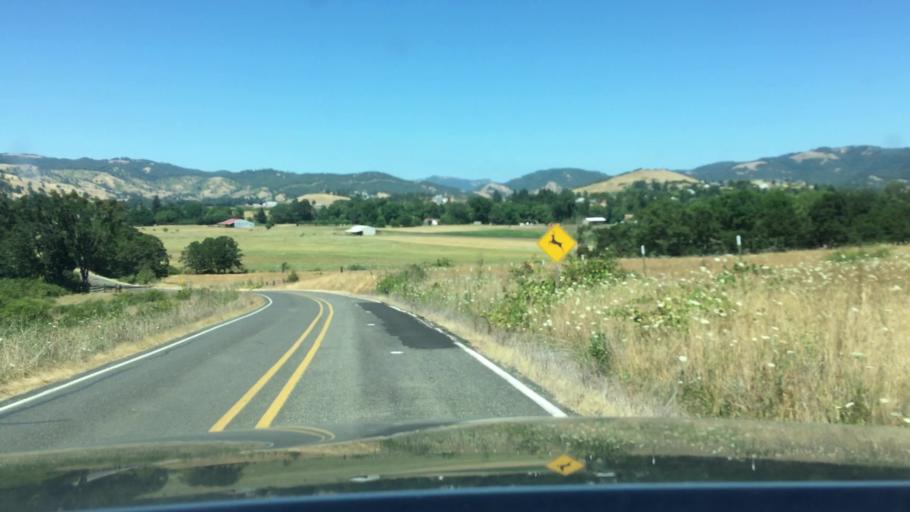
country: US
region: Oregon
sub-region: Douglas County
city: Winston
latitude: 43.1324
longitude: -123.4127
